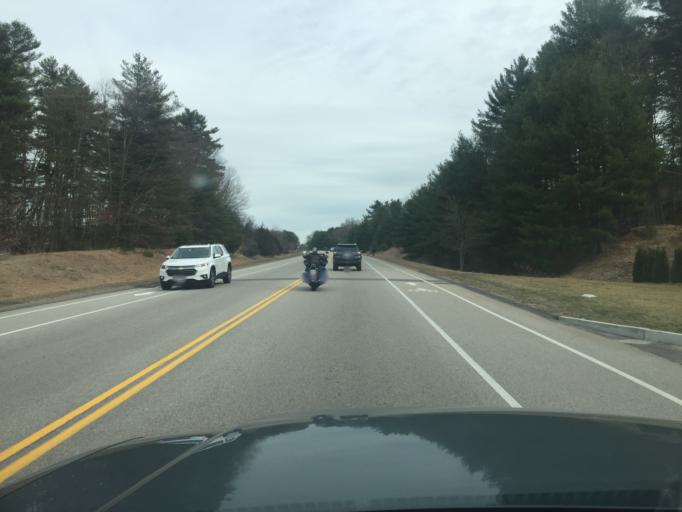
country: US
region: Massachusetts
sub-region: Norfolk County
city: Medfield
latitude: 42.1919
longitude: -71.3231
